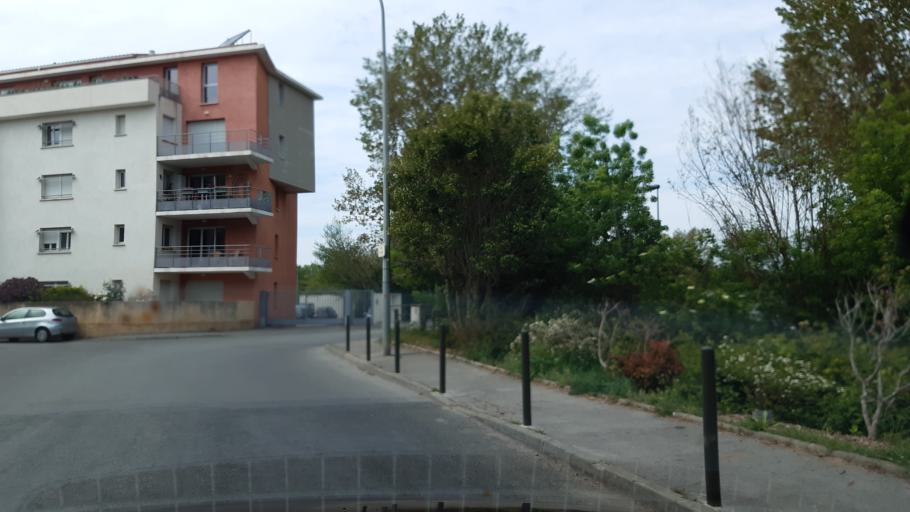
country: FR
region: Languedoc-Roussillon
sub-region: Departement de l'Aude
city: Narbonne
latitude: 43.1912
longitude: 2.9987
